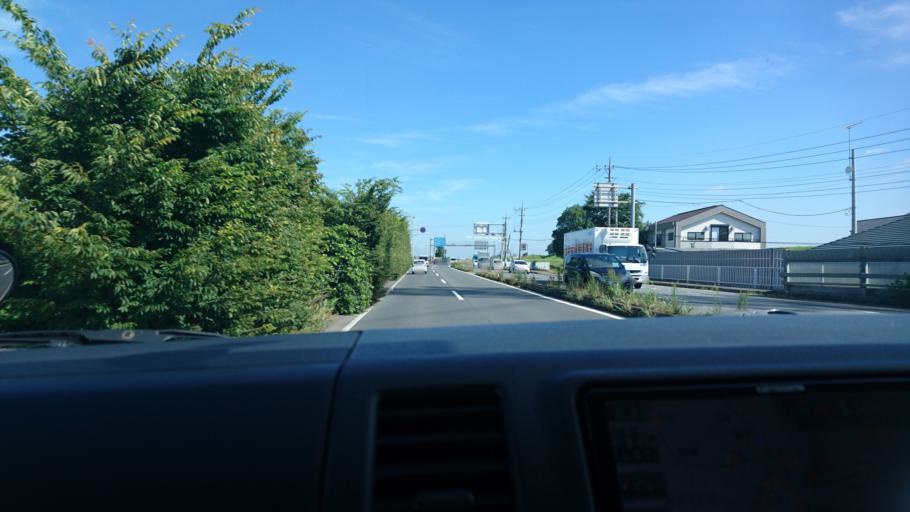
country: JP
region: Saitama
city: Kurihashi
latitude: 36.1344
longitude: 139.7068
